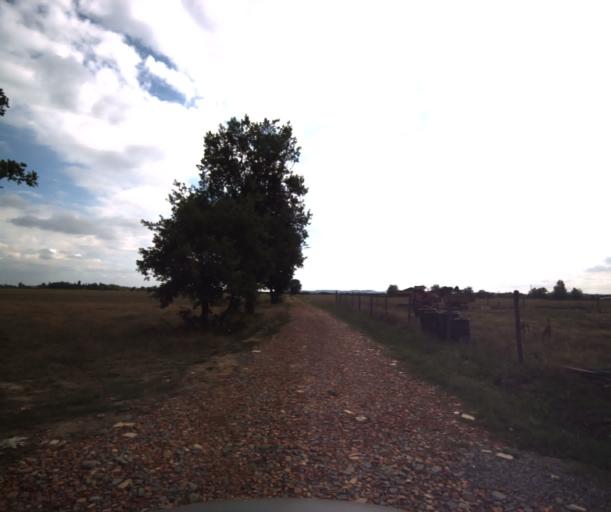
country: FR
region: Midi-Pyrenees
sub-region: Departement de la Haute-Garonne
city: Lherm
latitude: 43.3944
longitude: 1.2268
